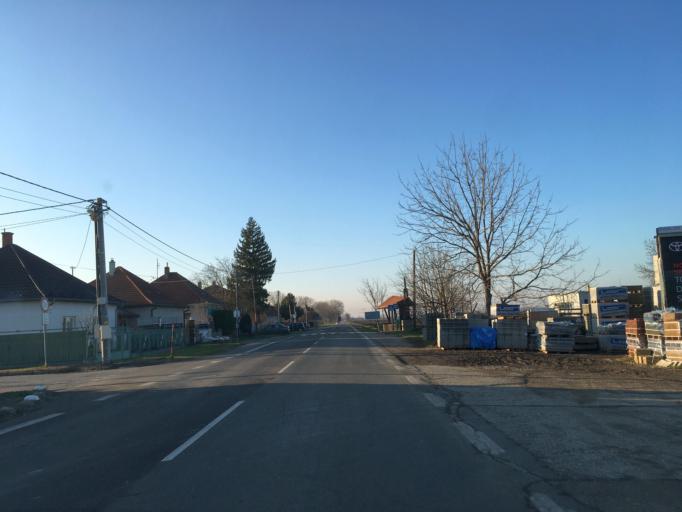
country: SK
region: Trnavsky
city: Gabcikovo
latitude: 47.8988
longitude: 17.5703
